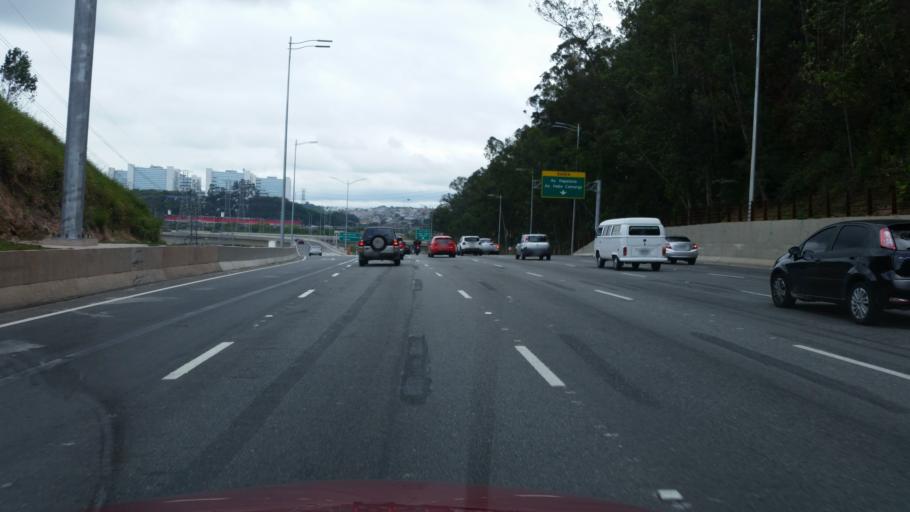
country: BR
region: Sao Paulo
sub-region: Taboao Da Serra
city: Taboao da Serra
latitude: -23.6386
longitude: -46.7249
